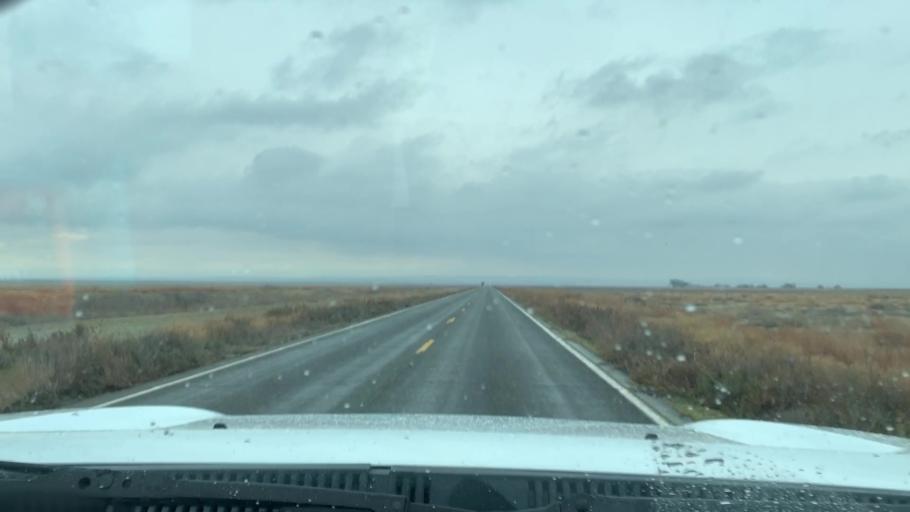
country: US
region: California
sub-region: Kings County
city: Kettleman City
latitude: 35.9341
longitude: -119.7910
